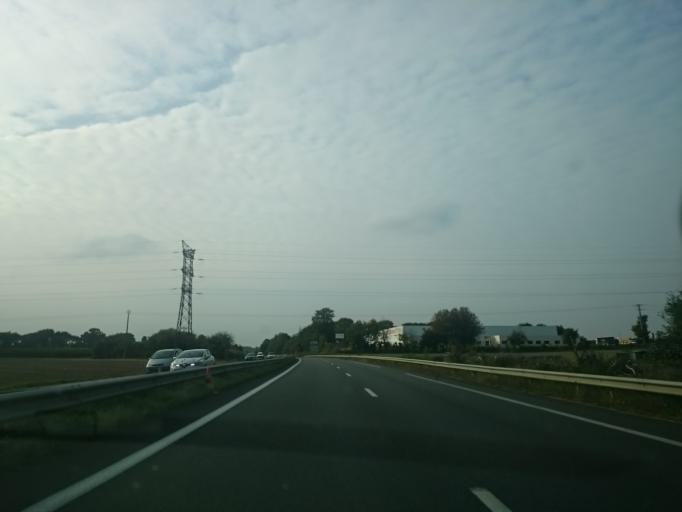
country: FR
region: Brittany
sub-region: Departement des Cotes-d'Armor
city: Graces
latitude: 48.5625
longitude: -3.1886
